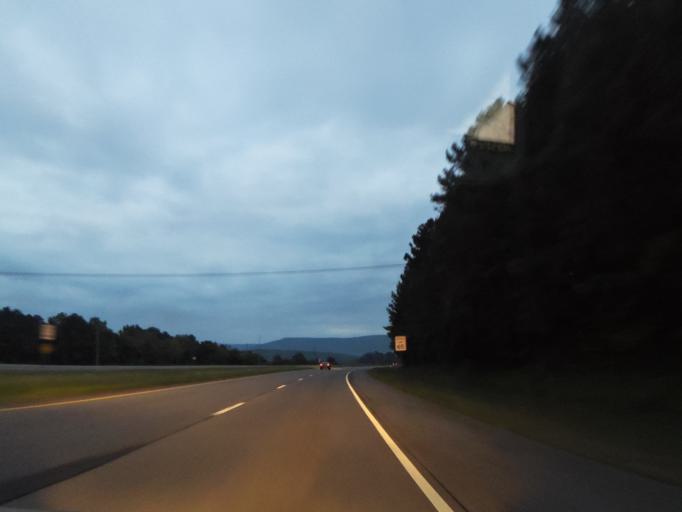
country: US
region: Alabama
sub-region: Madison County
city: Owens Cross Roads
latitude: 34.6942
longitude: -86.3615
